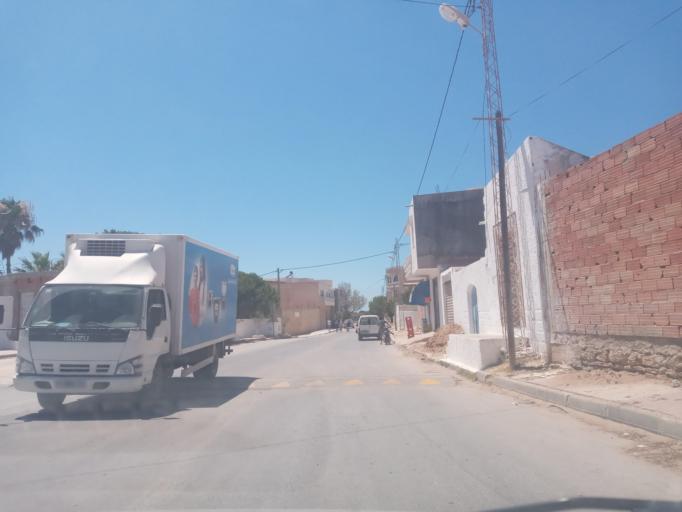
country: TN
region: Nabul
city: El Haouaria
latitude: 37.0487
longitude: 11.0075
